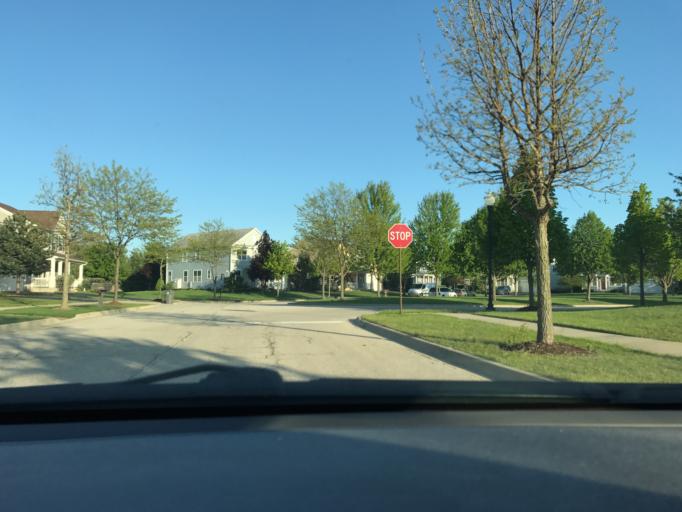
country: US
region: Illinois
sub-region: Kane County
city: Pingree Grove
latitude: 42.0361
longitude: -88.3586
